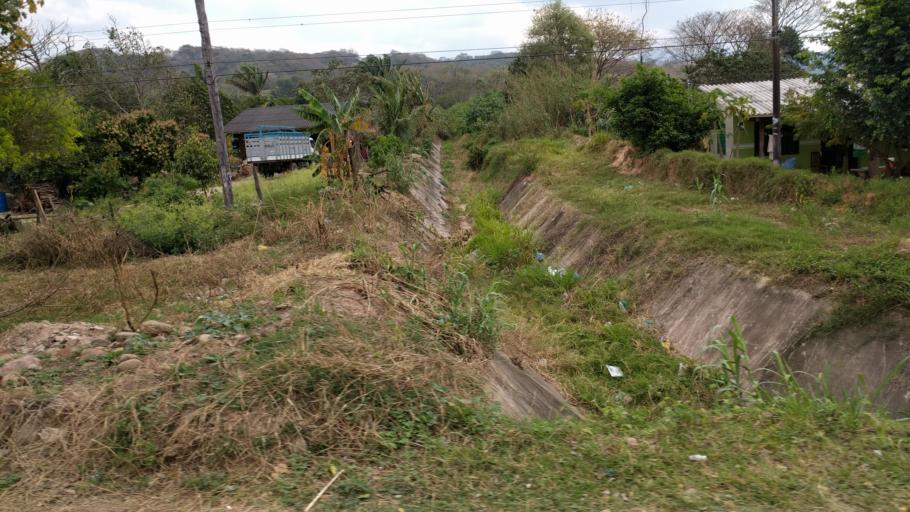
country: BO
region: Santa Cruz
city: Jorochito
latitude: -18.1192
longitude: -63.4623
